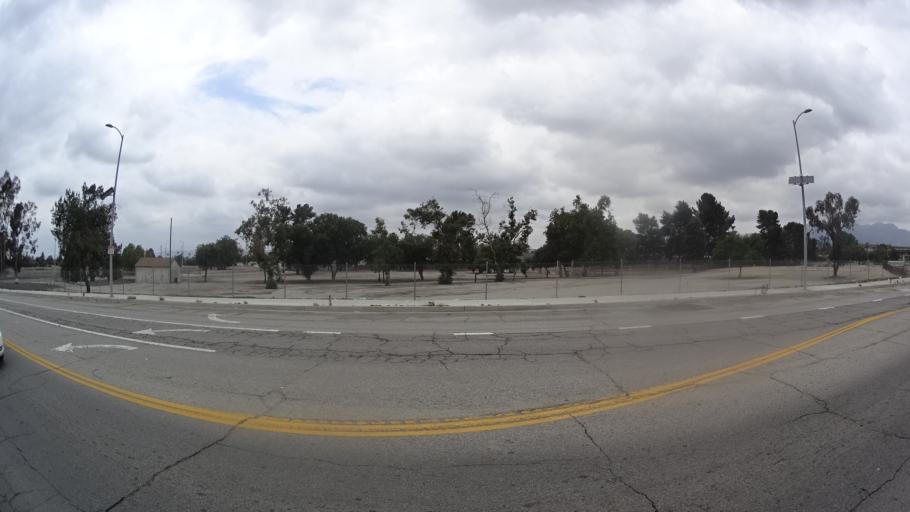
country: US
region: California
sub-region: Los Angeles County
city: San Fernando
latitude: 34.2605
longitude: -118.4445
